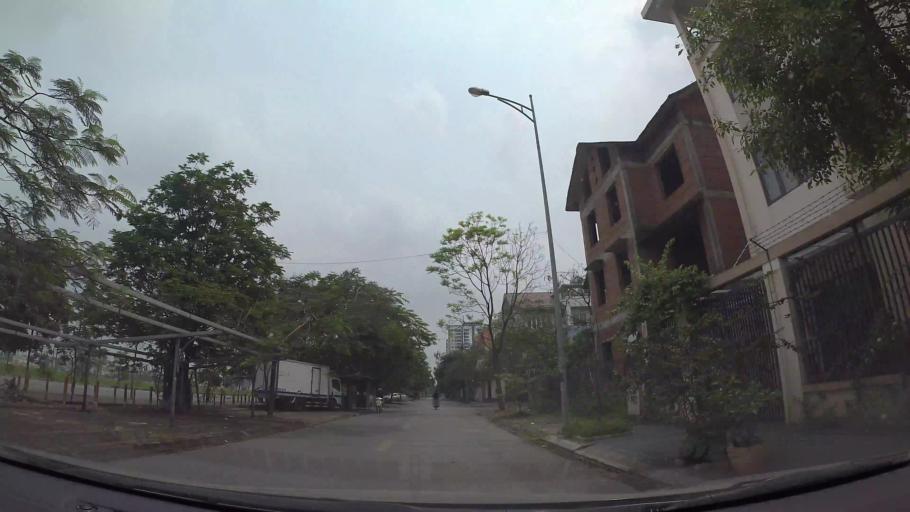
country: VN
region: Ha Noi
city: Trau Quy
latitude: 21.0682
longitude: 105.9107
